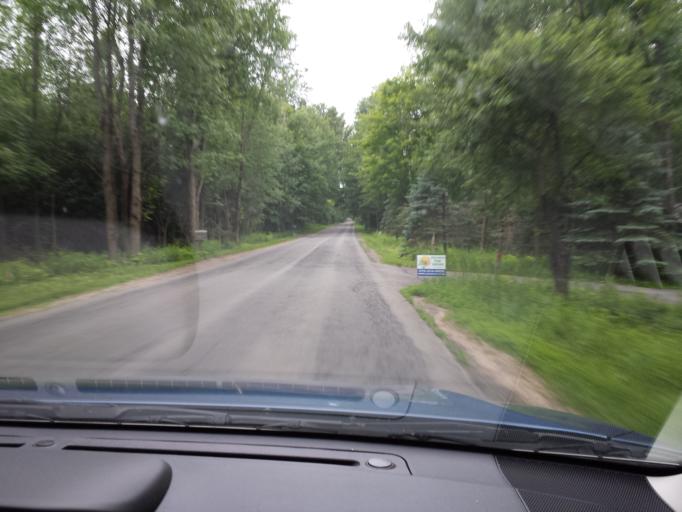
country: US
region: New York
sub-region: St. Lawrence County
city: Potsdam
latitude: 44.7113
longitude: -74.9549
